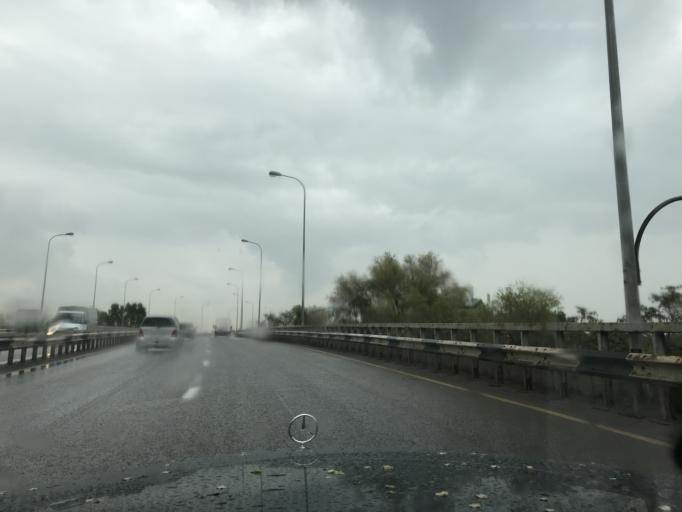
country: KZ
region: Almaty Oblysy
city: Pervomayskiy
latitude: 43.3355
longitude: 76.9632
